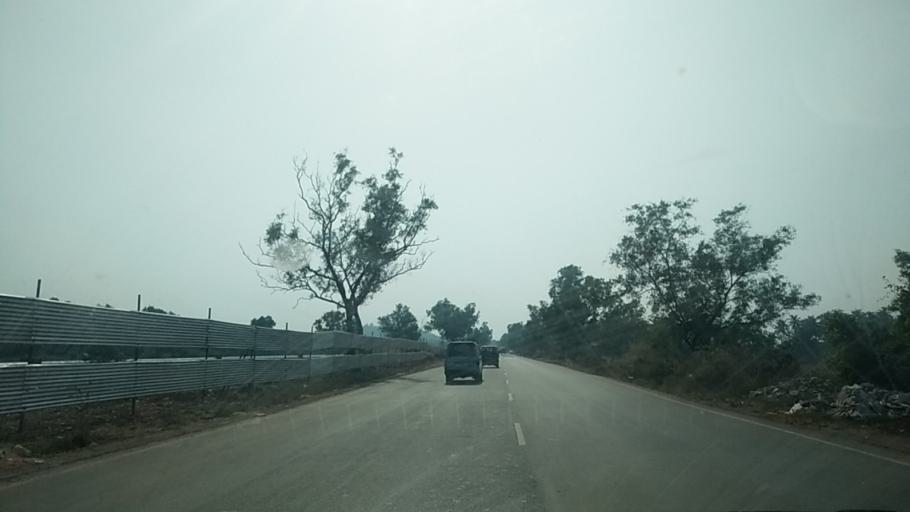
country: IN
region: Goa
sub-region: North Goa
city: Guirim
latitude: 15.5789
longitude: 73.8116
